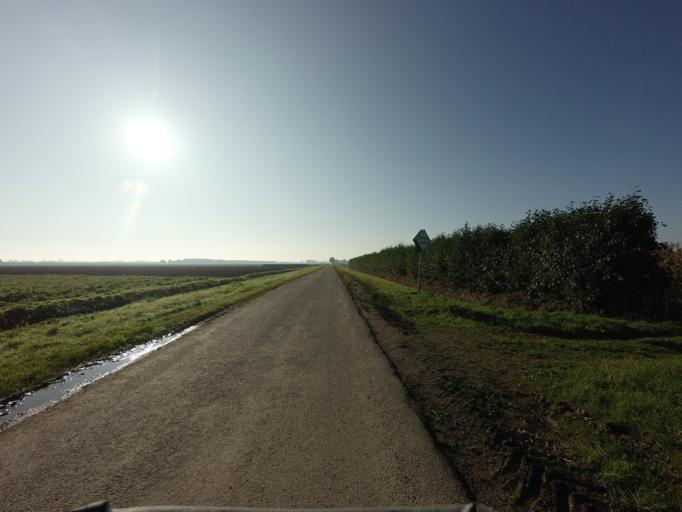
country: NL
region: North Brabant
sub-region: Gemeente Werkendam
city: Werkendam
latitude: 51.7916
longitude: 4.8814
